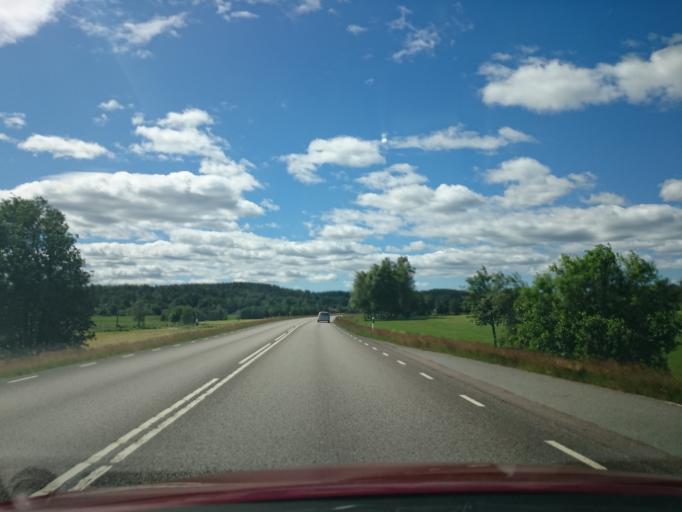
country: SE
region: Vaestra Goetaland
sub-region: Lerums Kommun
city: Olstorp
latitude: 57.8308
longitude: 12.2544
